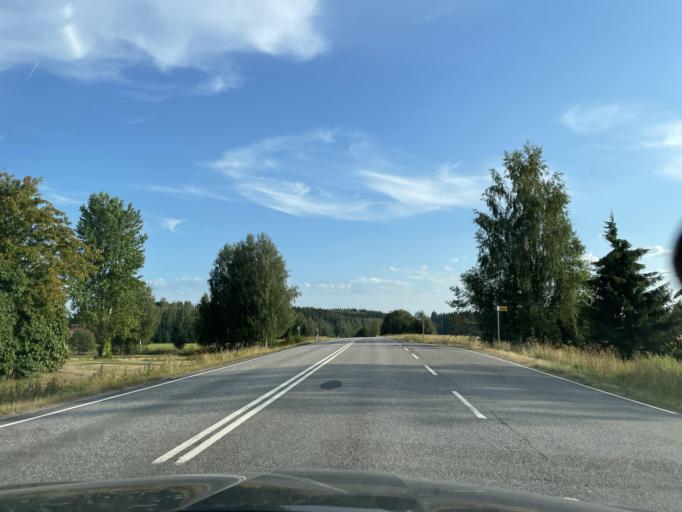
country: FI
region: Paijanne Tavastia
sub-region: Lahti
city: Auttoinen
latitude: 61.2968
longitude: 25.0879
